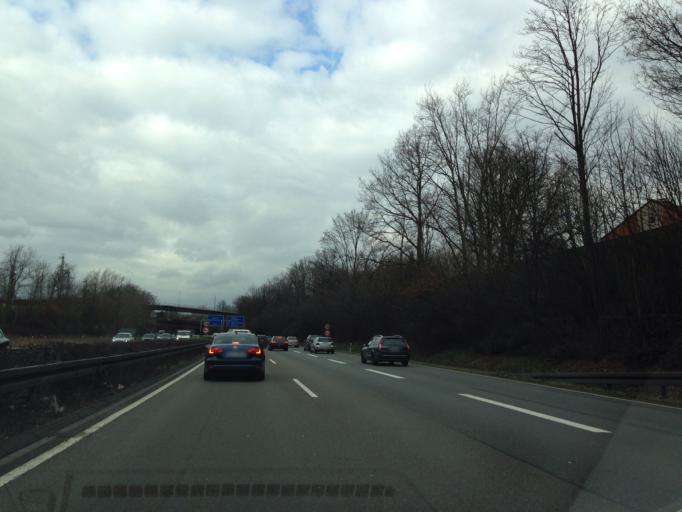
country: DE
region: North Rhine-Westphalia
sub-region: Regierungsbezirk Arnsberg
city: Herne
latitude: 51.5338
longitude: 7.2074
